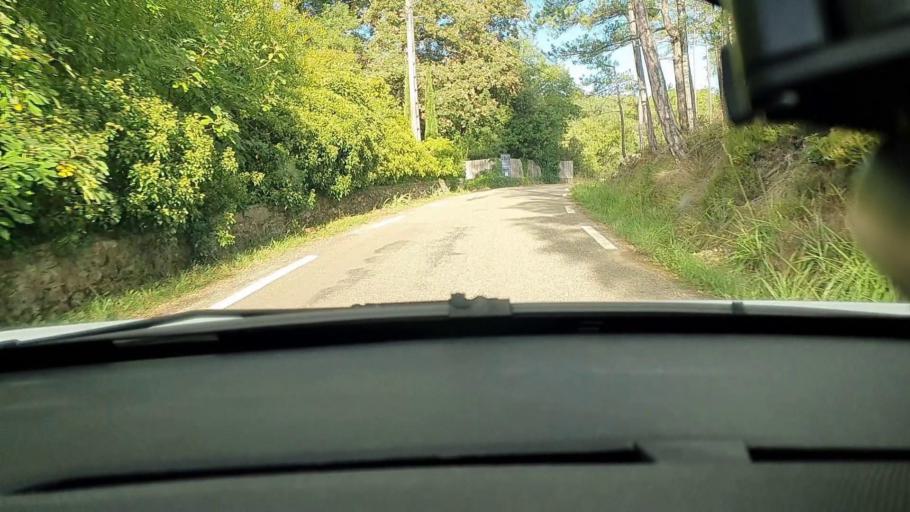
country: FR
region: Languedoc-Roussillon
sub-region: Departement du Gard
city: Besseges
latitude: 44.3223
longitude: 4.1204
